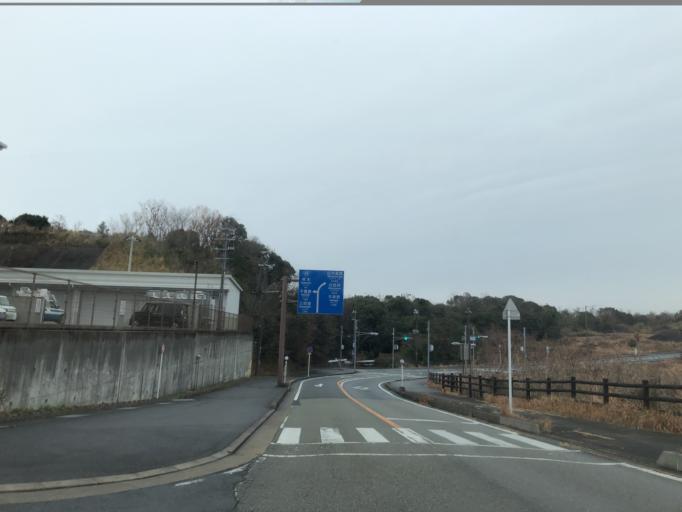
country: JP
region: Wakayama
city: Tanabe
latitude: 33.6667
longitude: 135.3577
